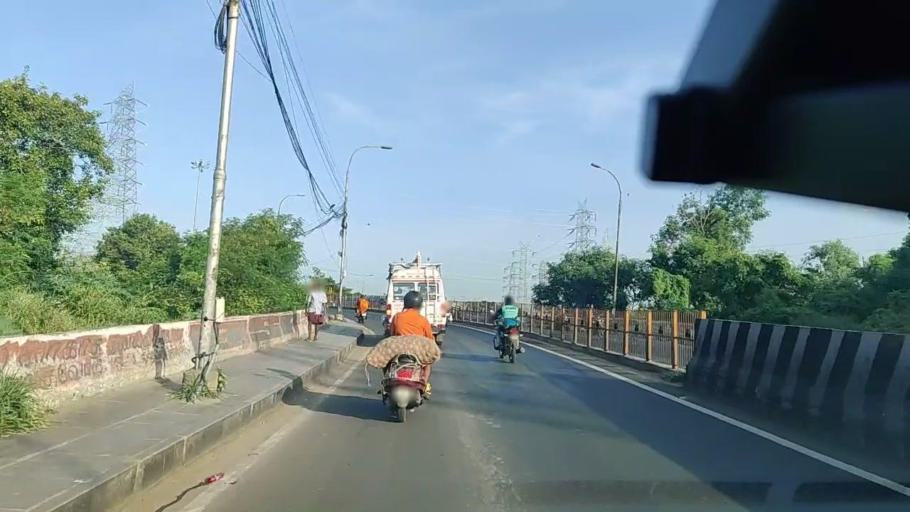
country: IN
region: Tamil Nadu
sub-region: Chennai
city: George Town
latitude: 13.1040
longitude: 80.2722
